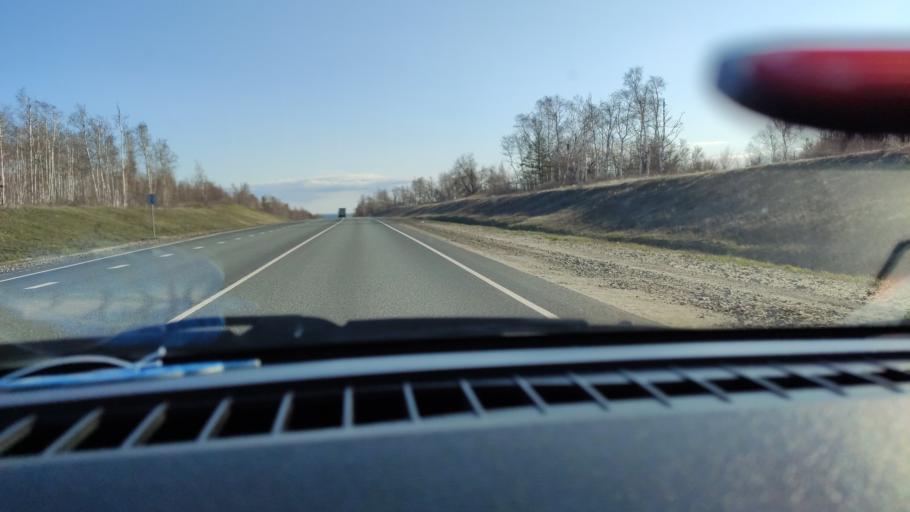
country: RU
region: Saratov
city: Khvalynsk
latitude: 52.5583
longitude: 48.0855
